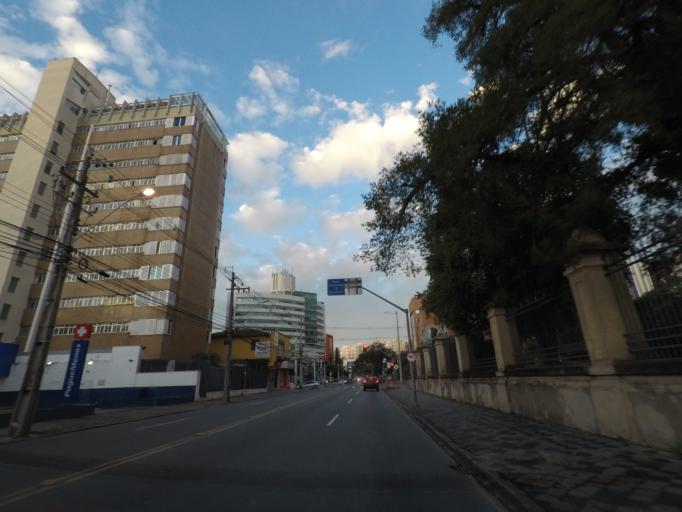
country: BR
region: Parana
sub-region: Curitiba
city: Curitiba
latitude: -25.4419
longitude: -49.2863
